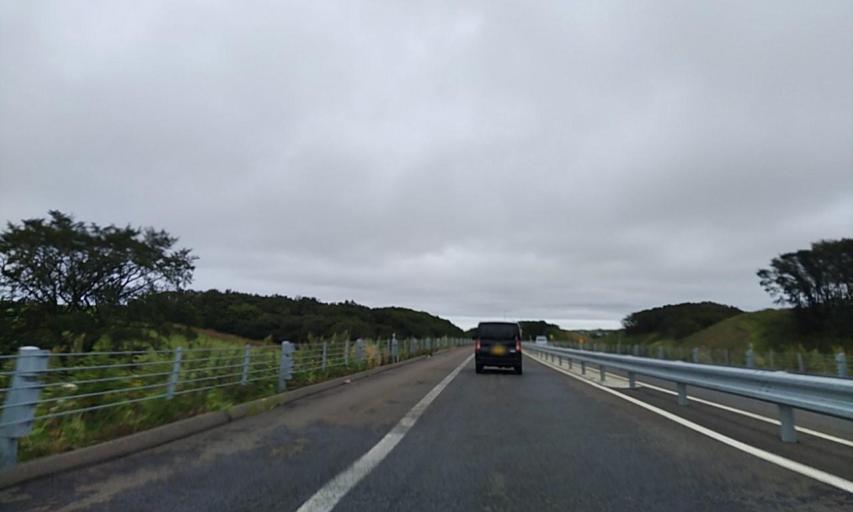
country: JP
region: Hokkaido
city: Nemuro
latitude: 43.2913
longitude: 145.5181
